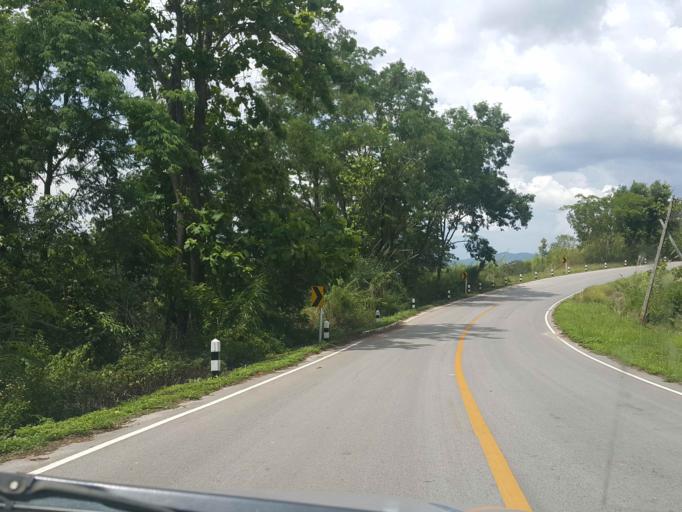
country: TH
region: Nan
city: Ban Luang
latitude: 18.8443
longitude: 100.3996
